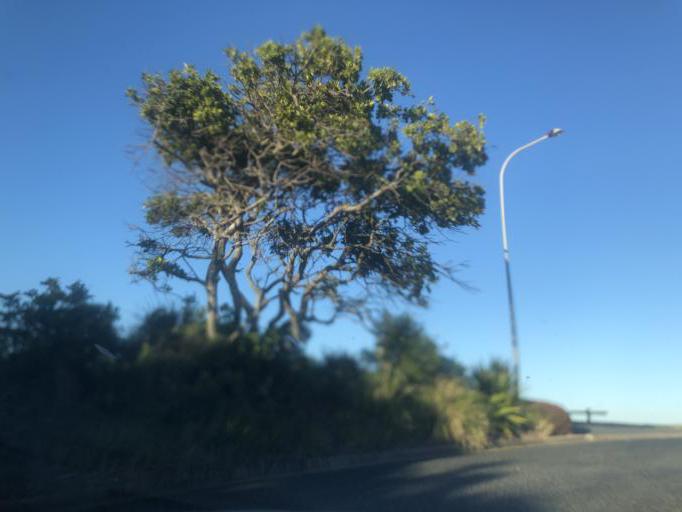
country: AU
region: New South Wales
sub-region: Coffs Harbour
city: Coffs Harbour
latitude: -30.3095
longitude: 153.1350
